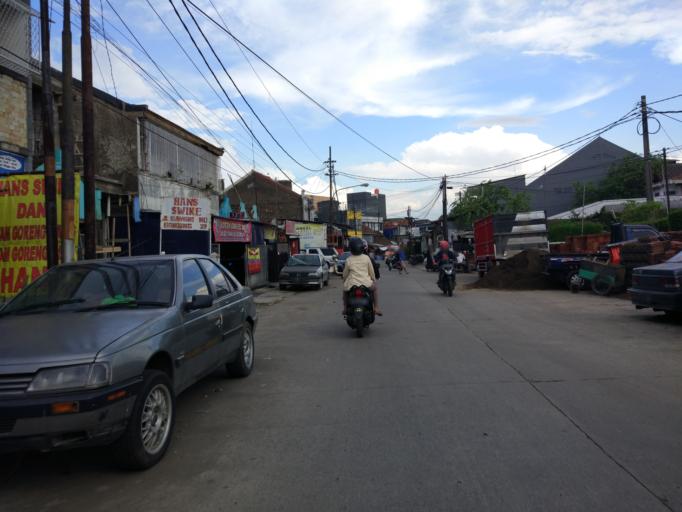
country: ID
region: West Java
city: Bandung
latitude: -6.9228
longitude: 107.5811
